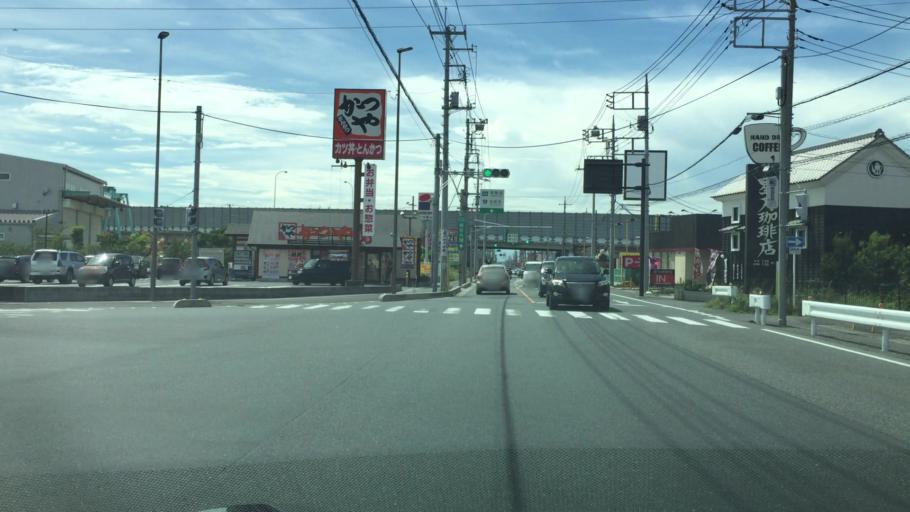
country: JP
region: Chiba
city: Nagareyama
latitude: 35.8470
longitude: 139.8753
